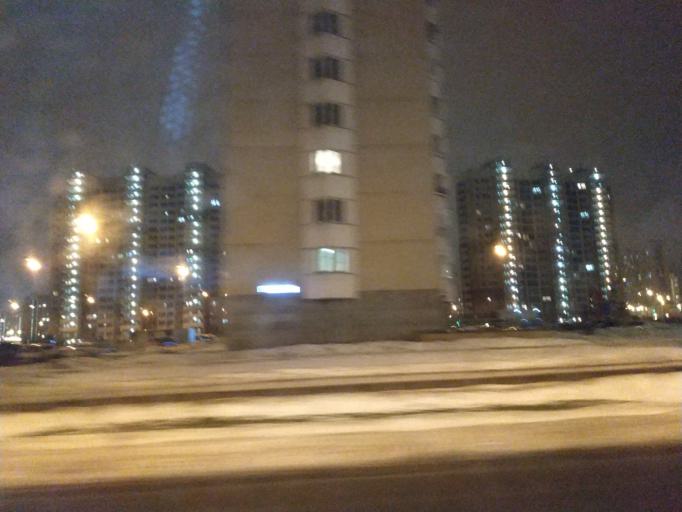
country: RU
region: Moscow
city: Nekrasovka
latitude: 55.7064
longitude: 37.9341
